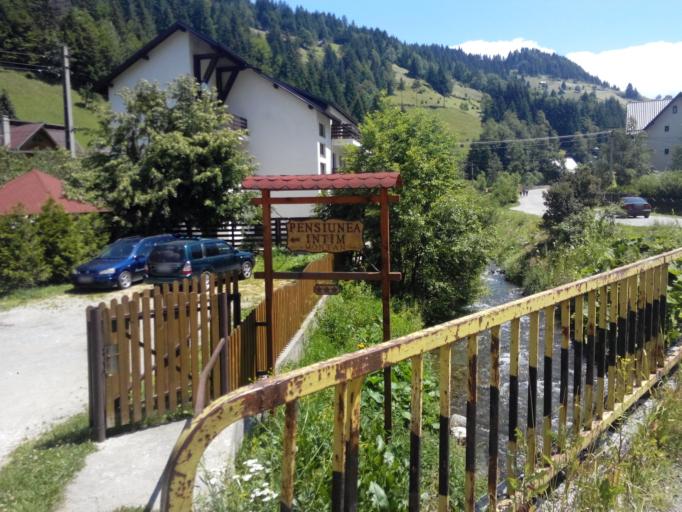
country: RO
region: Brasov
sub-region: Comuna Fundata
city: Fundata
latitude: 45.4517
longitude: 25.3257
